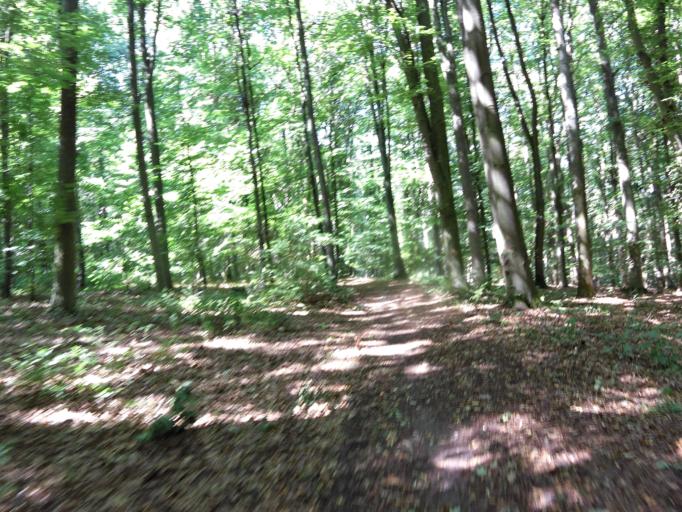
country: DE
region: Bavaria
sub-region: Regierungsbezirk Unterfranken
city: Theilheim
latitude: 49.7495
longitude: 10.0160
